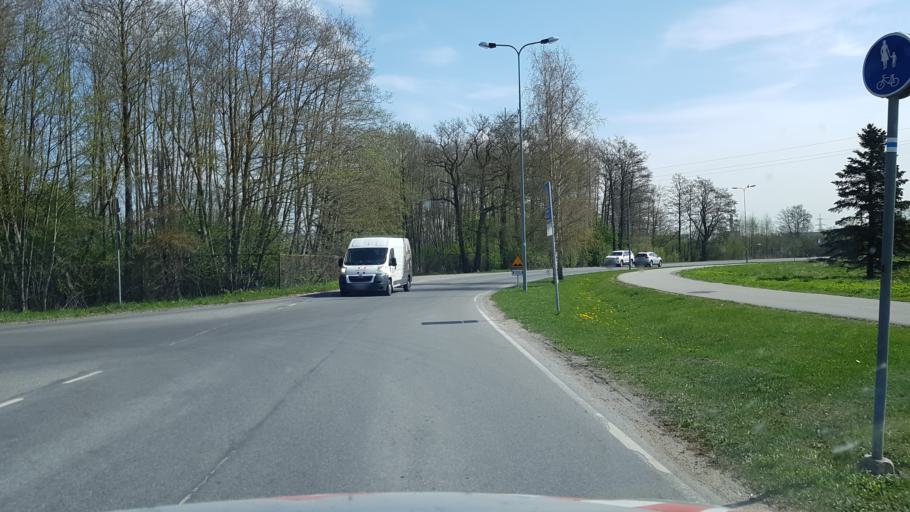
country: EE
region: Harju
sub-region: Saue vald
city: Laagri
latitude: 59.4124
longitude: 24.6070
